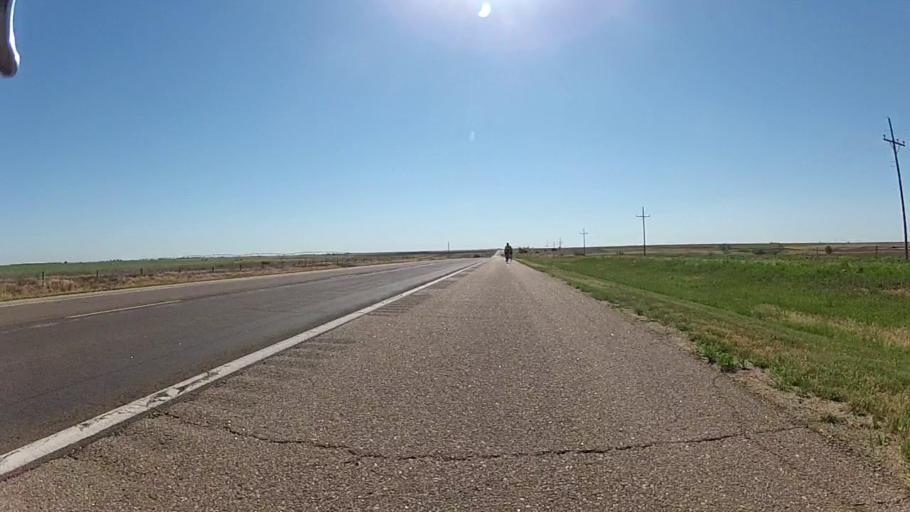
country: US
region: Kansas
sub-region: Kiowa County
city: Greensburg
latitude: 37.5862
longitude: -99.5490
